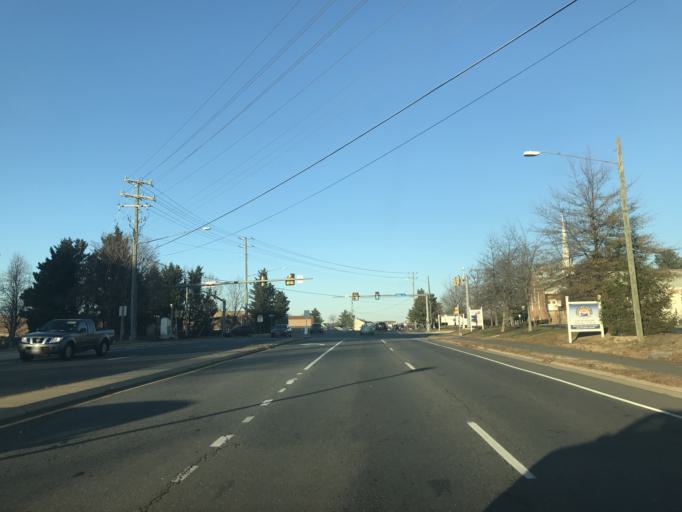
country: US
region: Virginia
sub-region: Fairfax County
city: Franconia
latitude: 38.7685
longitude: -77.1546
